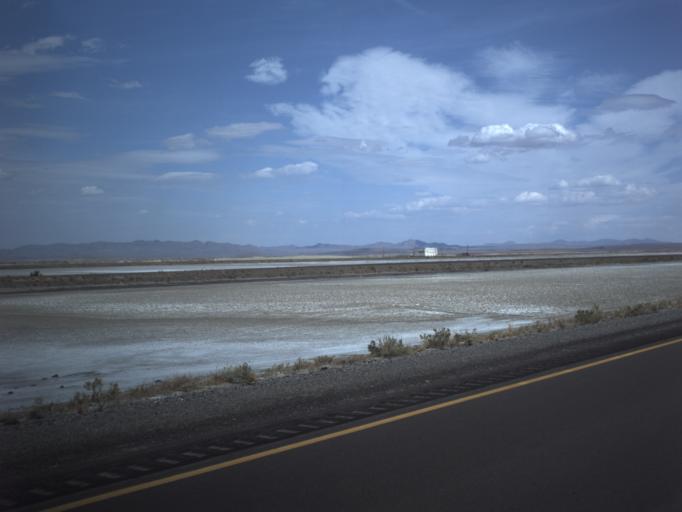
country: US
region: Utah
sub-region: Tooele County
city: Wendover
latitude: 40.7272
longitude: -113.3020
